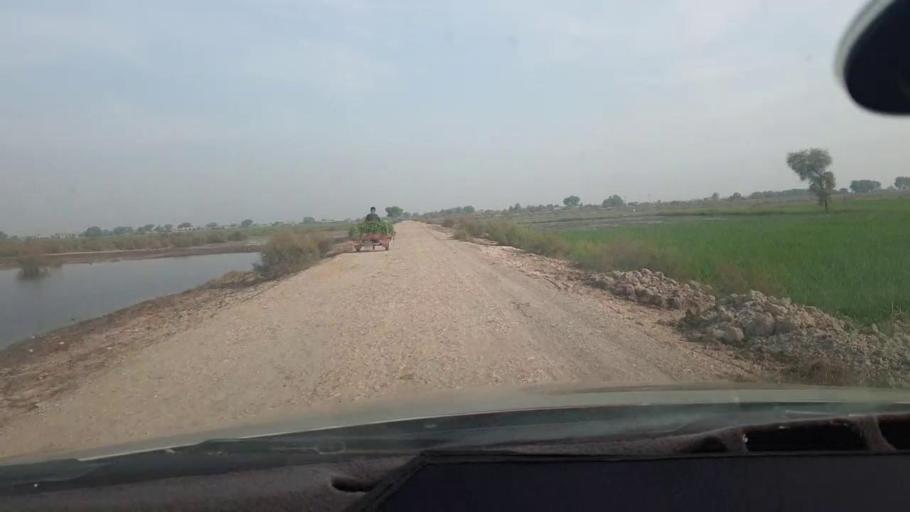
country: PK
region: Balochistan
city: Jhatpat
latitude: 28.3628
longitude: 68.4063
